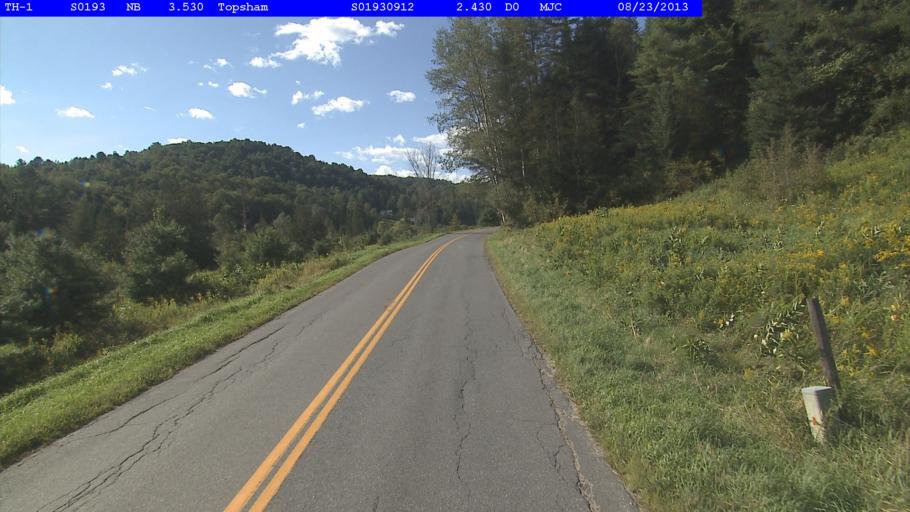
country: US
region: New Hampshire
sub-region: Grafton County
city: Haverhill
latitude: 44.1027
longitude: -72.2306
